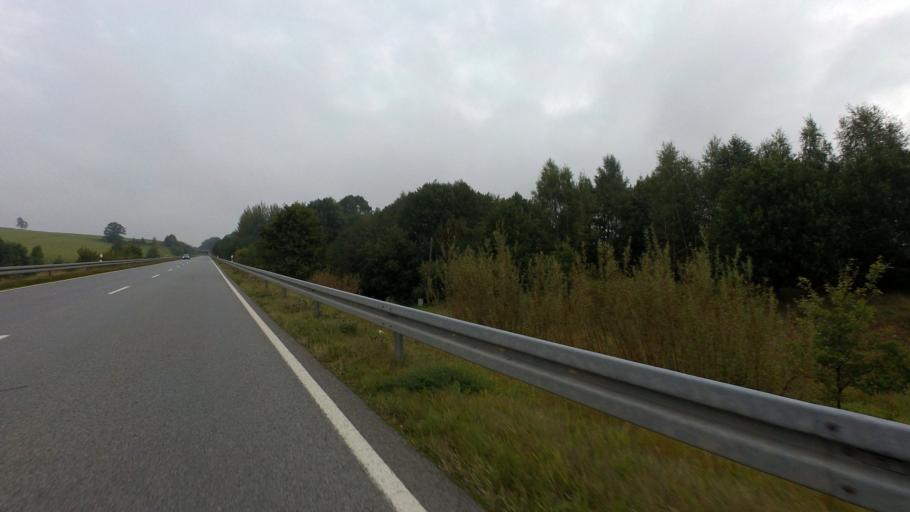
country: DE
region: Saxony
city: Berthelsdorf
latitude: 51.0473
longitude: 14.2118
